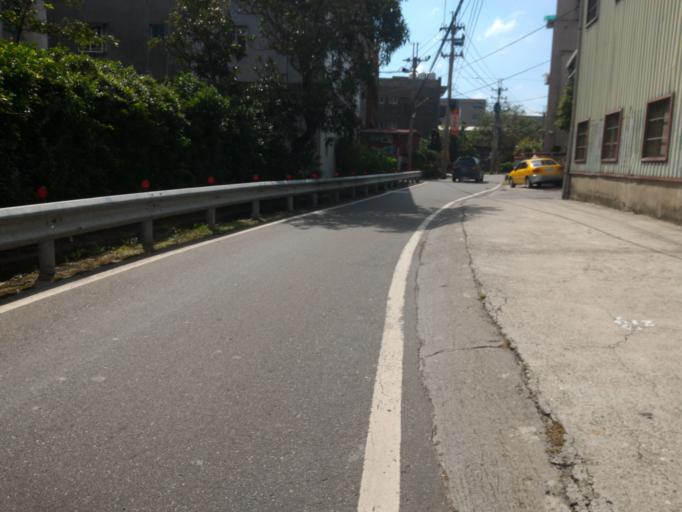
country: TW
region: Taiwan
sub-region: Taoyuan
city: Taoyuan
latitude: 24.9626
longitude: 121.3955
